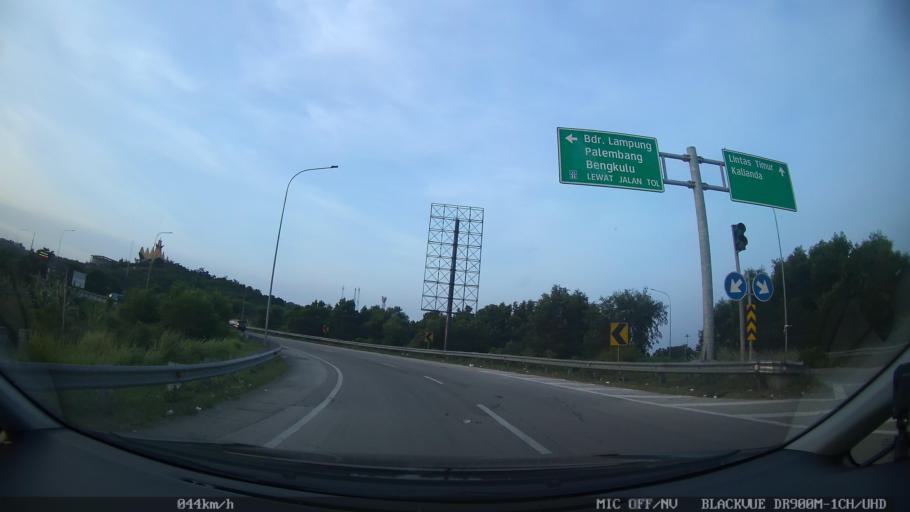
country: ID
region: Lampung
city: Penengahan
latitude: -5.8700
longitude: 105.7510
